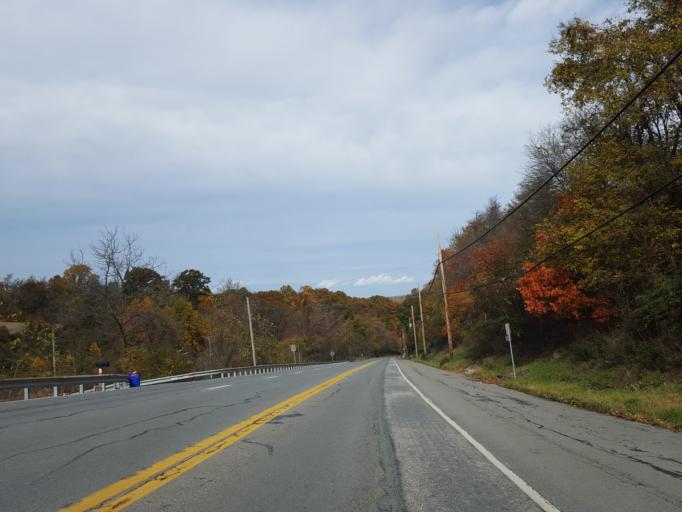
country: US
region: Pennsylvania
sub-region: York County
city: Wrightsville
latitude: 40.0033
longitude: -76.5421
